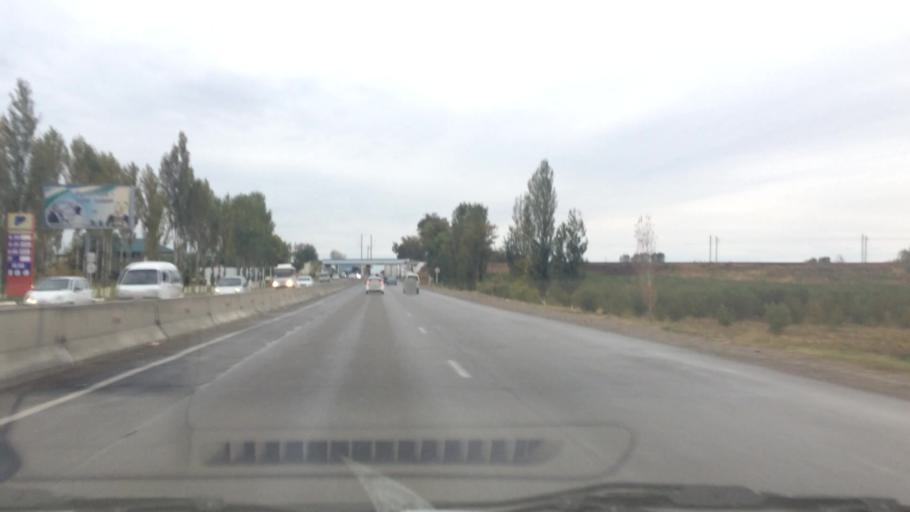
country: UZ
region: Toshkent
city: Urtaowul
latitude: 41.2092
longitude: 69.1197
